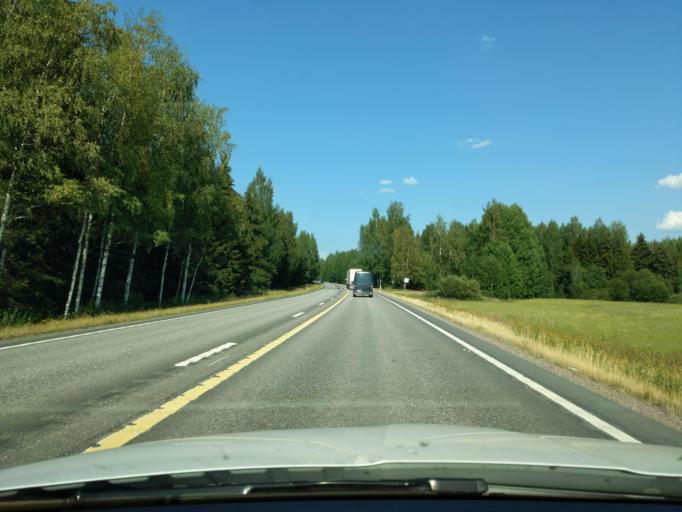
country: FI
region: Paijanne Tavastia
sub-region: Lahti
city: Jaervelae
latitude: 60.9022
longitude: 25.3167
